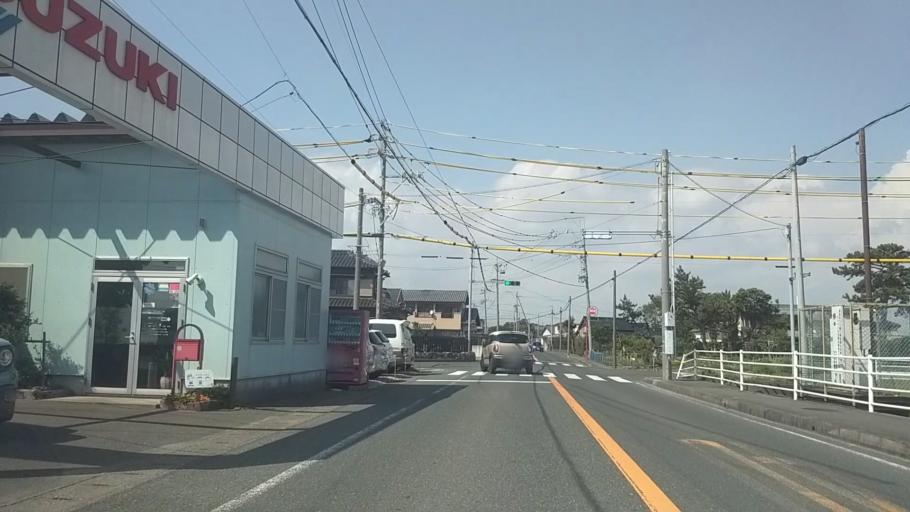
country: JP
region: Shizuoka
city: Hamamatsu
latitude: 34.6752
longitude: 137.7073
